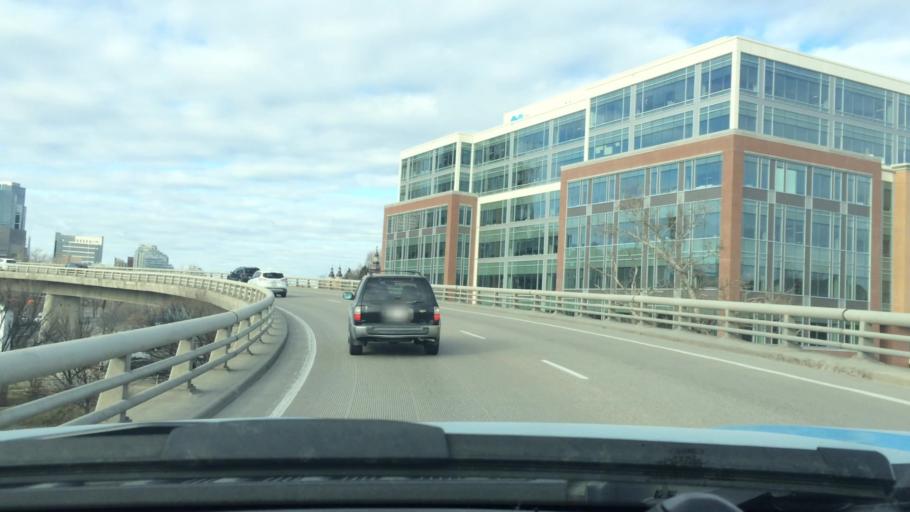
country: CA
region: Alberta
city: Calgary
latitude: 51.0506
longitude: -114.0487
